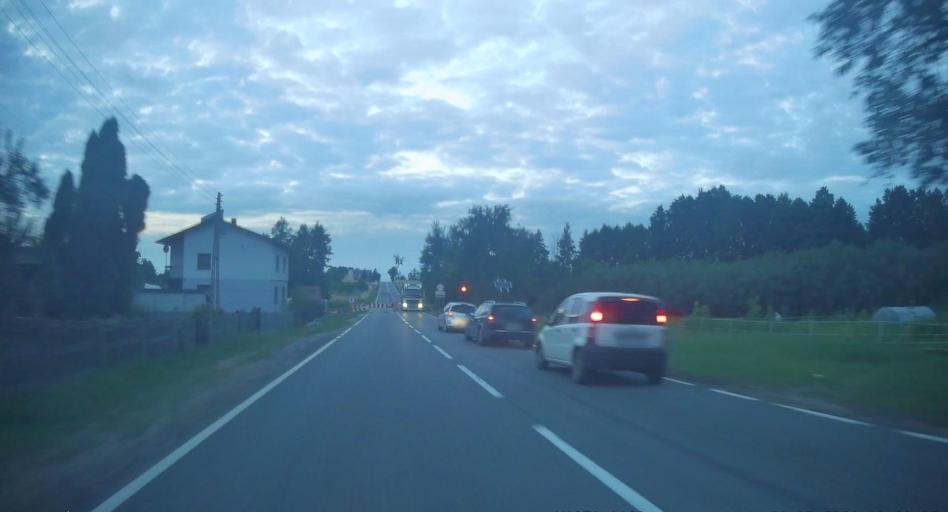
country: PL
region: Opole Voivodeship
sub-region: Powiat oleski
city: Dalachow
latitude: 51.0455
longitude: 18.5969
